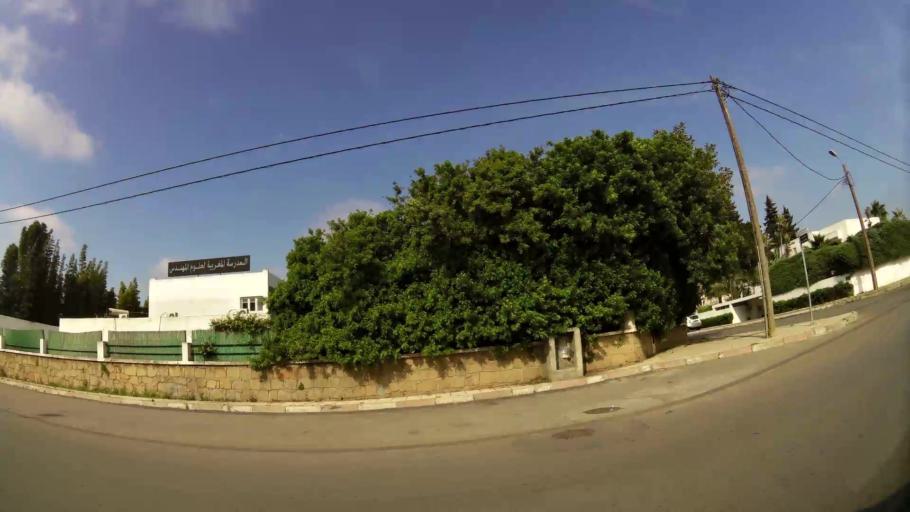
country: MA
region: Rabat-Sale-Zemmour-Zaer
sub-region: Rabat
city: Rabat
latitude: 33.9677
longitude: -6.8385
